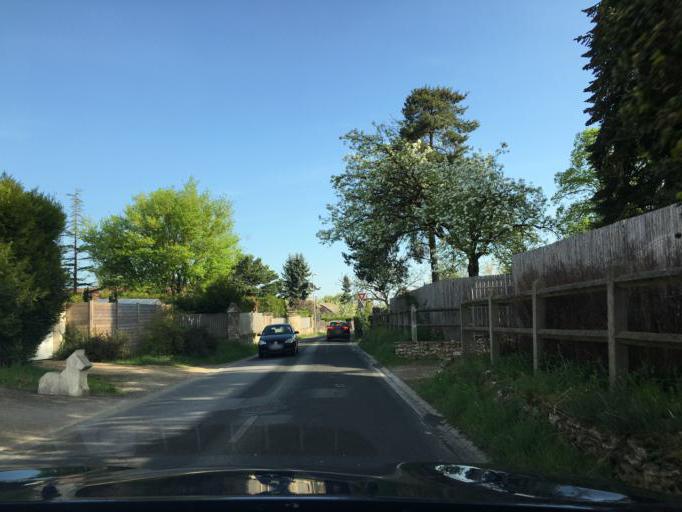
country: FR
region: Ile-de-France
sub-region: Departement des Yvelines
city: Conde-sur-Vesgre
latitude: 48.7413
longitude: 1.6678
